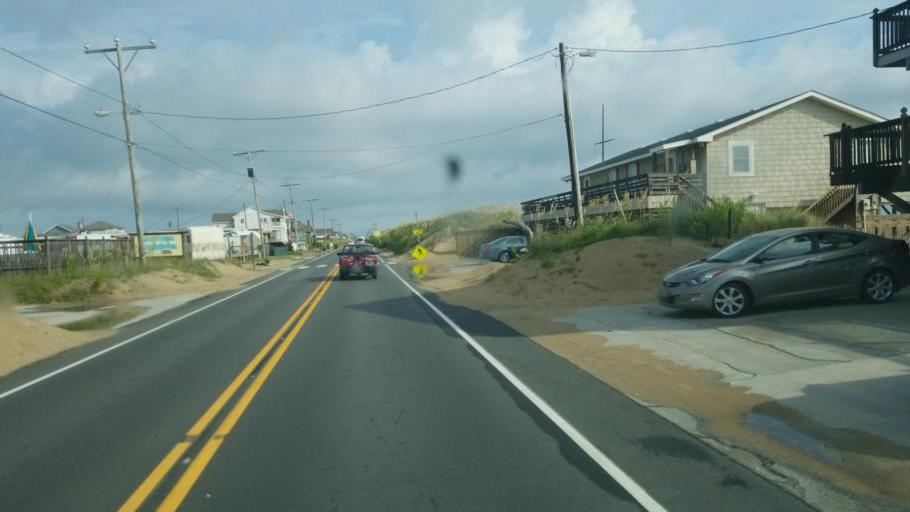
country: US
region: North Carolina
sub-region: Dare County
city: Kitty Hawk
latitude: 36.0556
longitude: -75.6829
